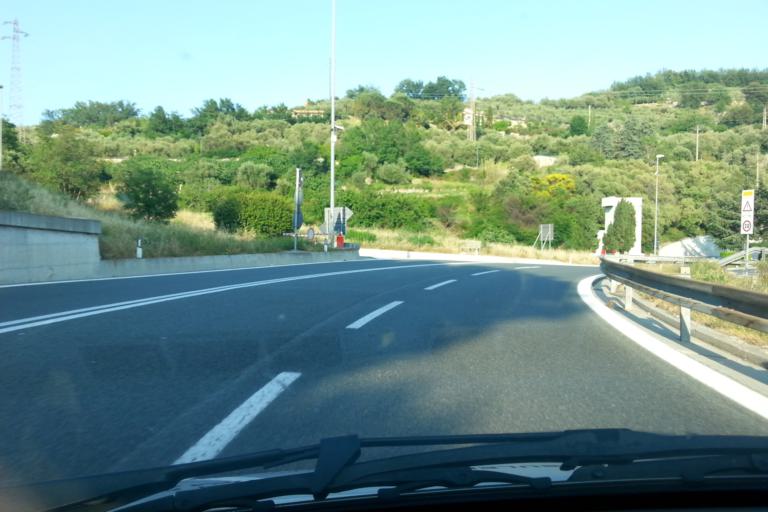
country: IT
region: Liguria
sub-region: Provincia di Savona
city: Pietra Ligure
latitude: 44.1558
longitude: 8.2699
